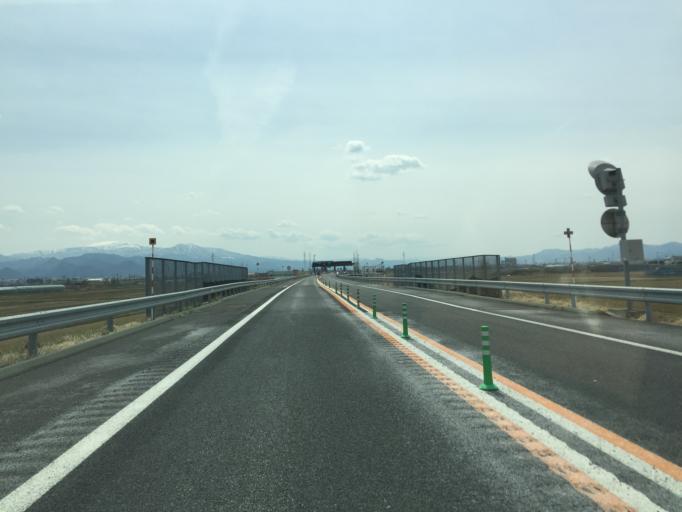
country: JP
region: Yamagata
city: Tendo
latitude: 38.3735
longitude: 140.3472
